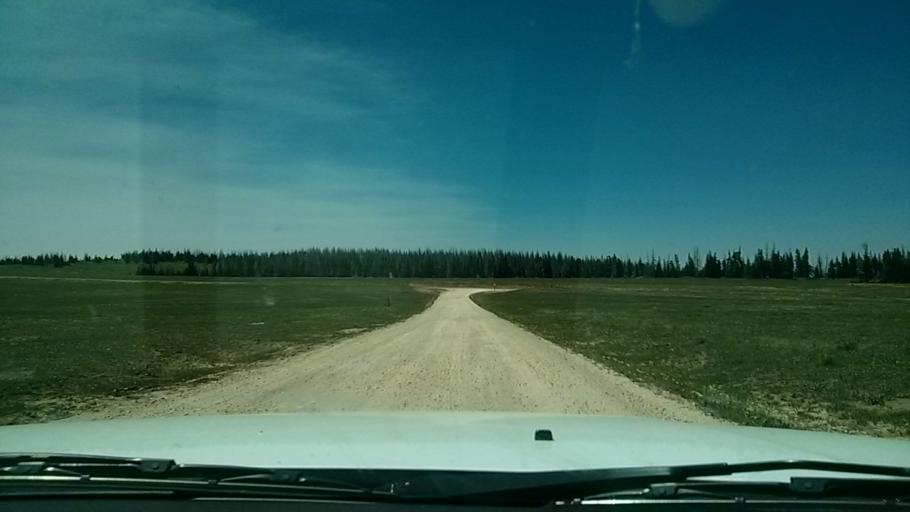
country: US
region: Utah
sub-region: Iron County
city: Parowan
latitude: 37.6709
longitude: -112.8370
